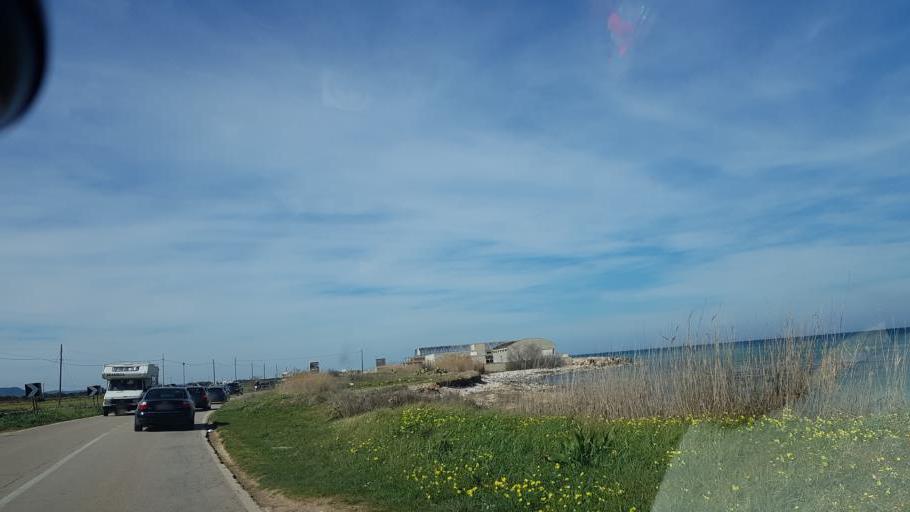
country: IT
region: Apulia
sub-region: Provincia di Brindisi
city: Pezze di Greco
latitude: 40.8586
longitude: 17.4330
